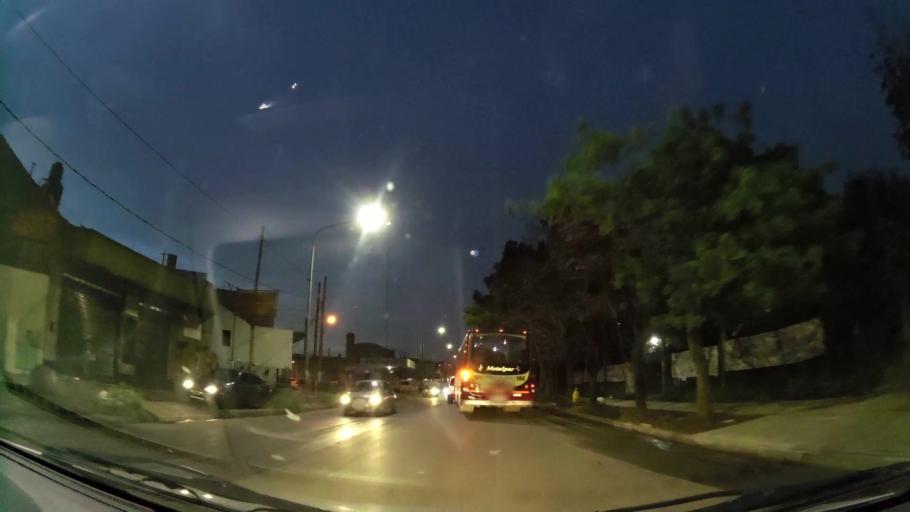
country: AR
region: Buenos Aires
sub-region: Partido de Lanus
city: Lanus
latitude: -34.7329
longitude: -58.3502
